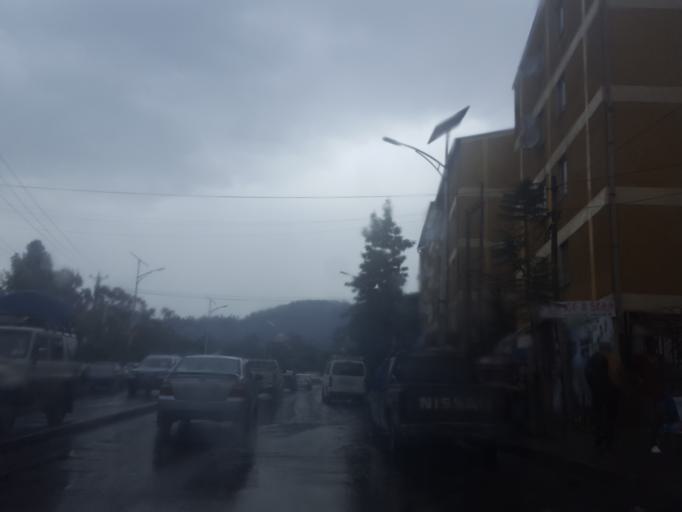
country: ET
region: Adis Abeba
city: Addis Ababa
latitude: 9.0272
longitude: 38.7831
